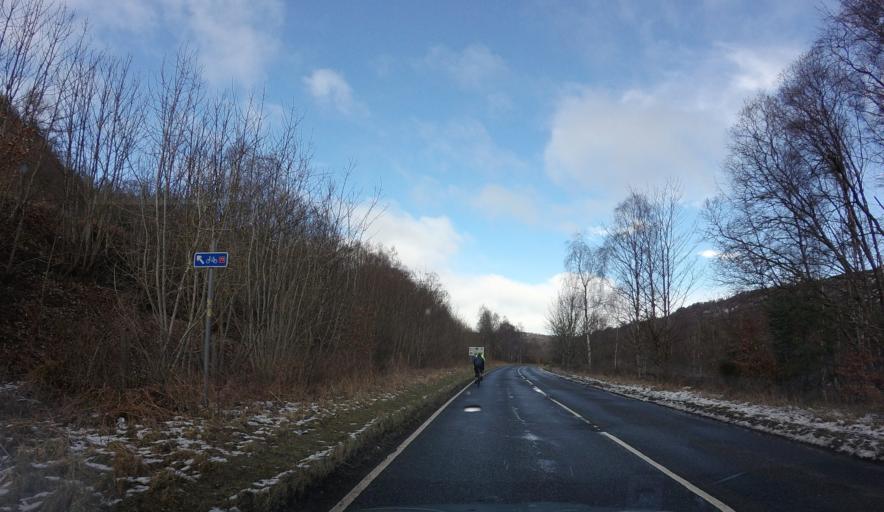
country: GB
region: Scotland
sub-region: Perth and Kinross
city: Bankfoot
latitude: 56.5483
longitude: -3.5627
